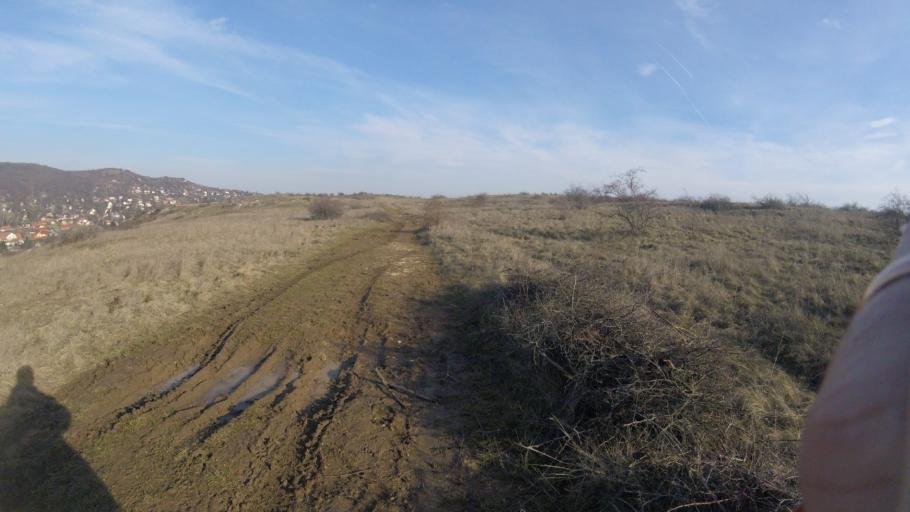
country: HU
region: Pest
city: Nagykovacsi
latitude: 47.6474
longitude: 18.9938
